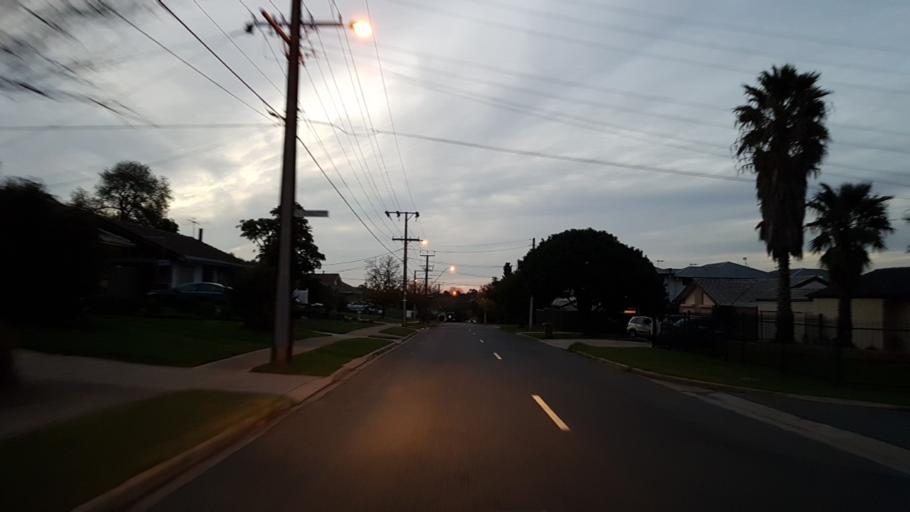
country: AU
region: South Australia
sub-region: Port Adelaide Enfield
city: Gilles Plains
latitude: -34.8505
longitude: 138.6653
